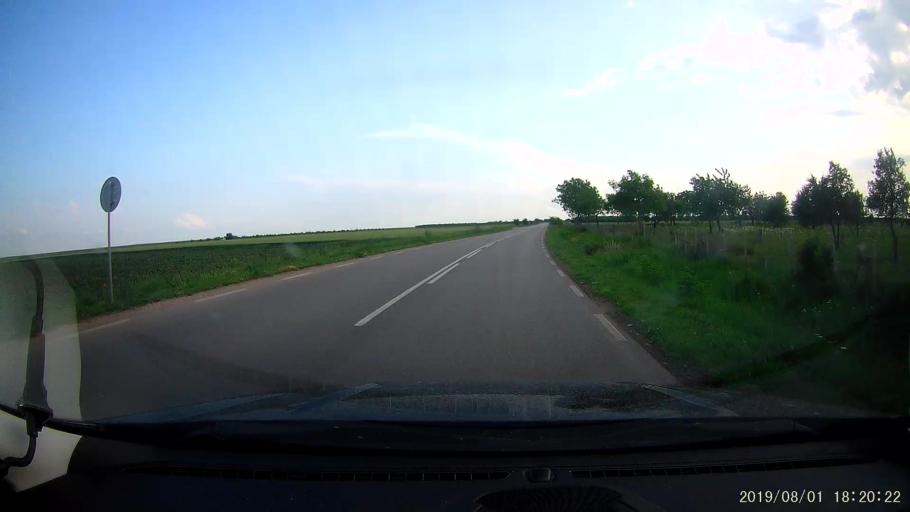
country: BG
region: Shumen
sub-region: Obshtina Kaolinovo
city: Kaolinovo
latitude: 43.6725
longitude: 27.0893
